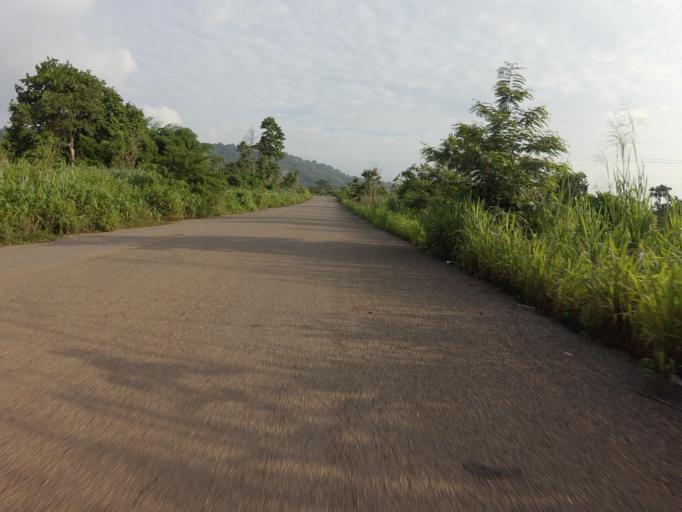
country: TG
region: Plateaux
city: Kpalime
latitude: 6.9298
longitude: 0.4622
